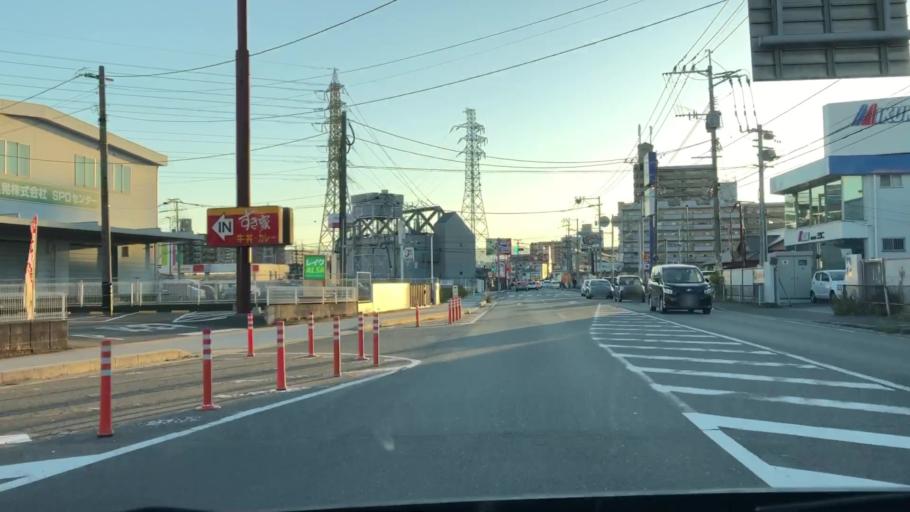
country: JP
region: Fukuoka
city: Fukuoka-shi
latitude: 33.6241
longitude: 130.4389
